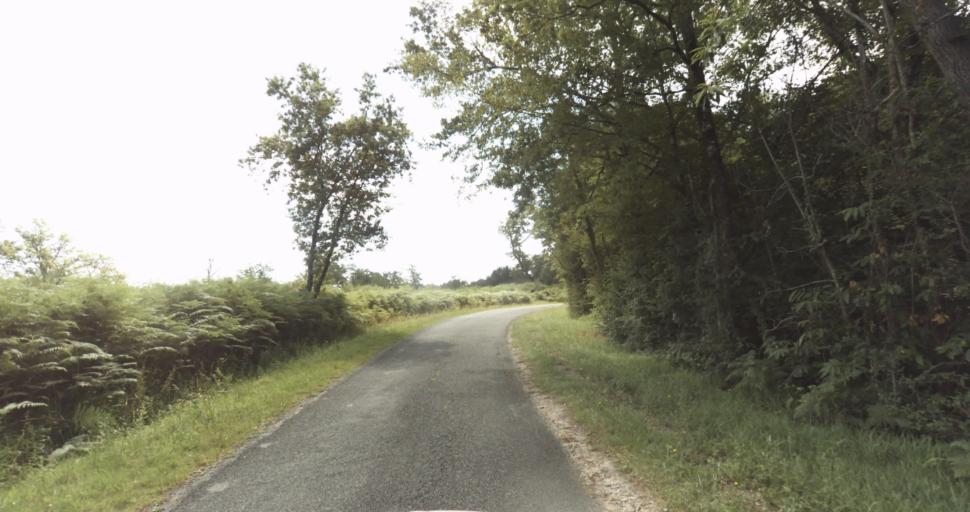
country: FR
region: Aquitaine
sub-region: Departement de la Gironde
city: Bazas
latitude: 44.4595
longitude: -0.2170
